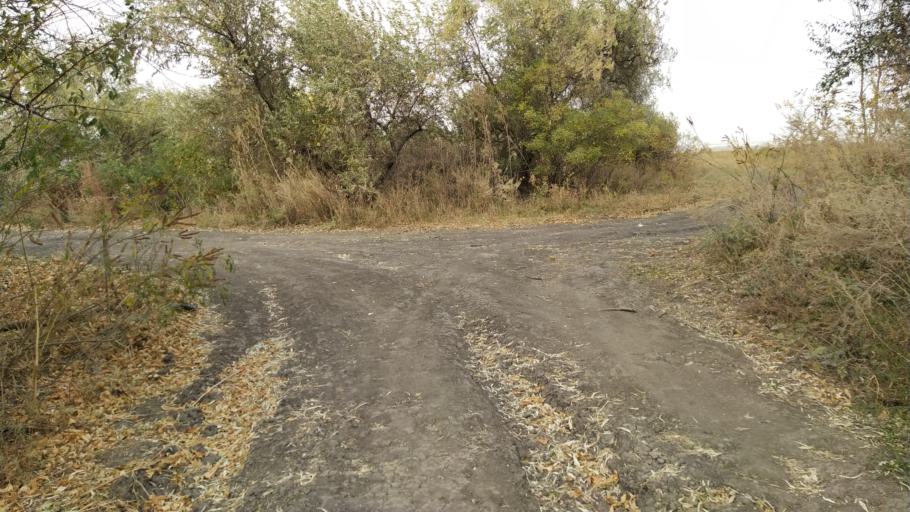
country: RU
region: Rostov
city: Kuleshovka
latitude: 47.1465
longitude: 39.5864
